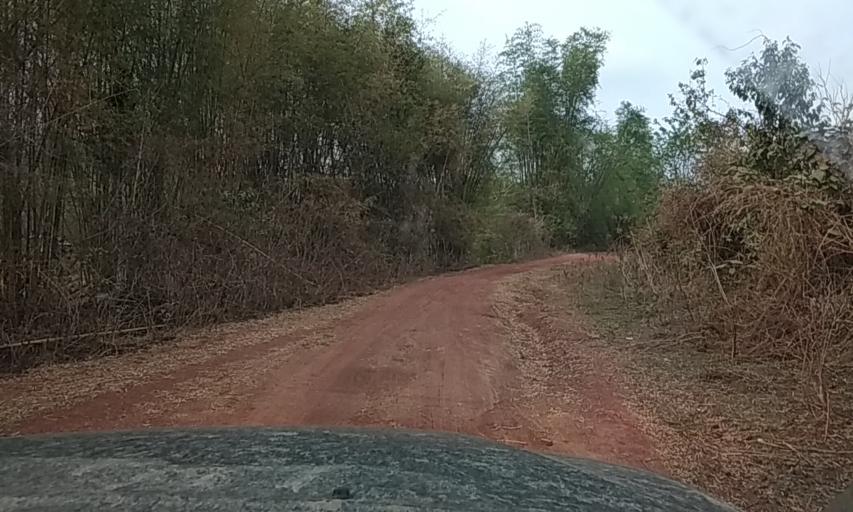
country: TH
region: Nan
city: Mae Charim
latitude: 18.4271
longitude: 101.1743
